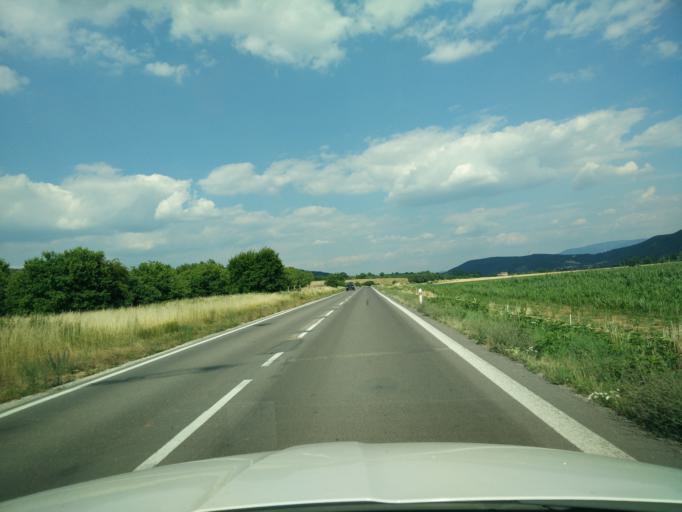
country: SK
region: Nitriansky
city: Partizanske
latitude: 48.7075
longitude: 18.4125
